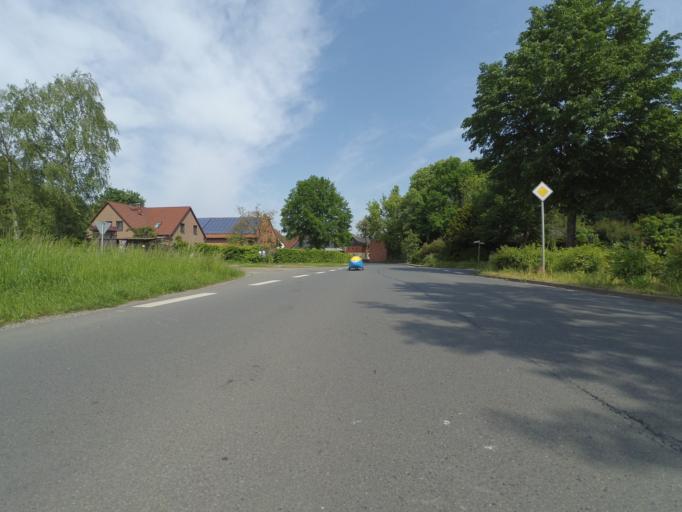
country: DE
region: Lower Saxony
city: Hohenhameln
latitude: 52.2656
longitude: 10.0508
